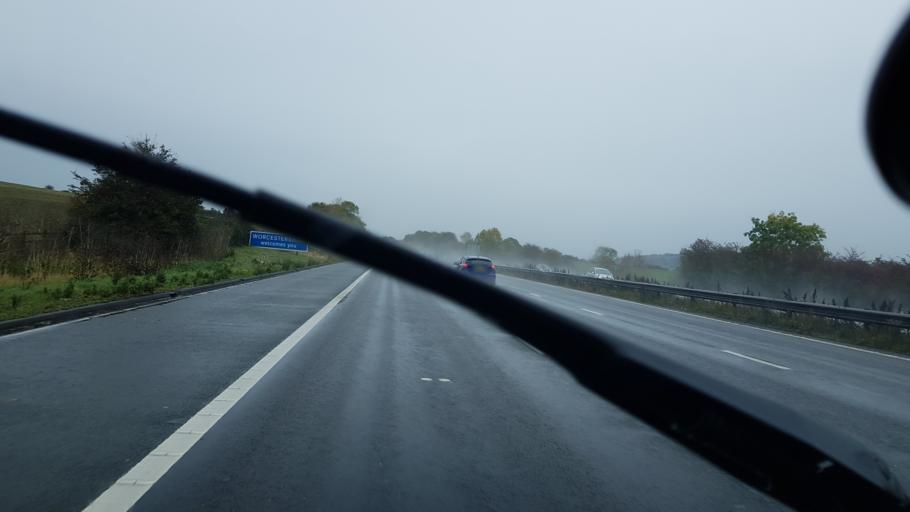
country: GB
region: England
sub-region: Worcestershire
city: Bredon
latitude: 52.0123
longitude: -2.1211
